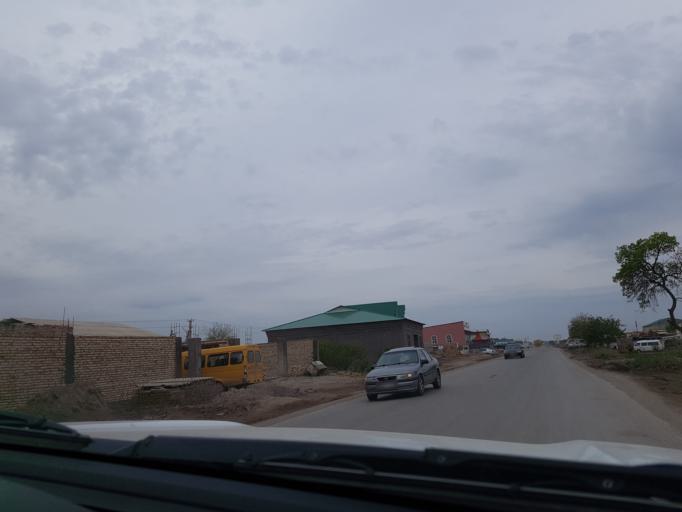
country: TM
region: Lebap
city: Turkmenabat
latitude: 39.0659
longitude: 63.5646
